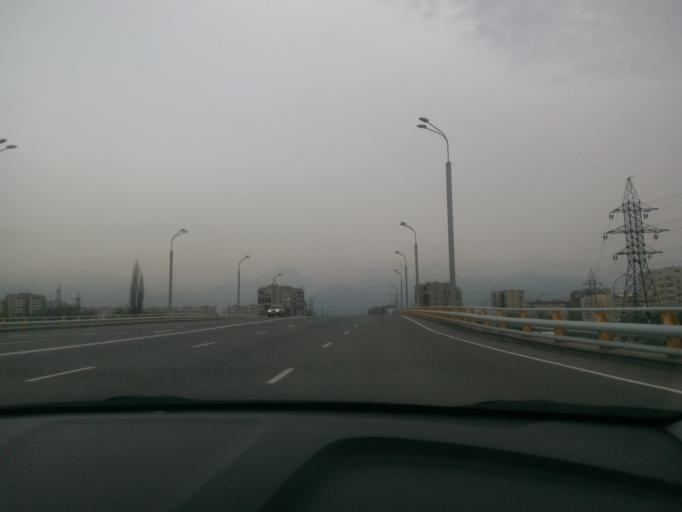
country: KZ
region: Almaty Qalasy
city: Almaty
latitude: 43.2447
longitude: 76.8274
